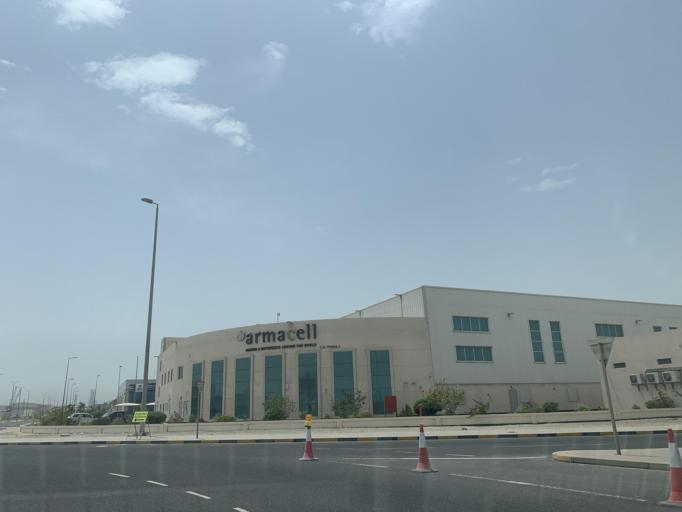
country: BH
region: Muharraq
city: Al Hadd
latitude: 26.2211
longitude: 50.6790
